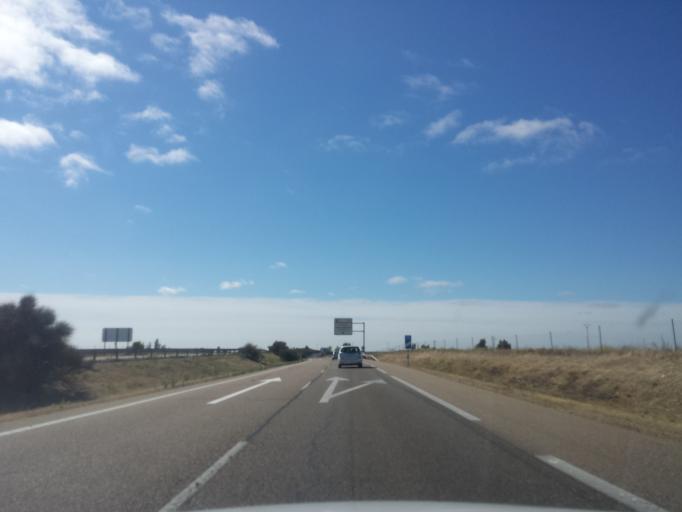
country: ES
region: Castille and Leon
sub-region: Provincia de Valladolid
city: Uruena
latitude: 41.6827
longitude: -5.2099
